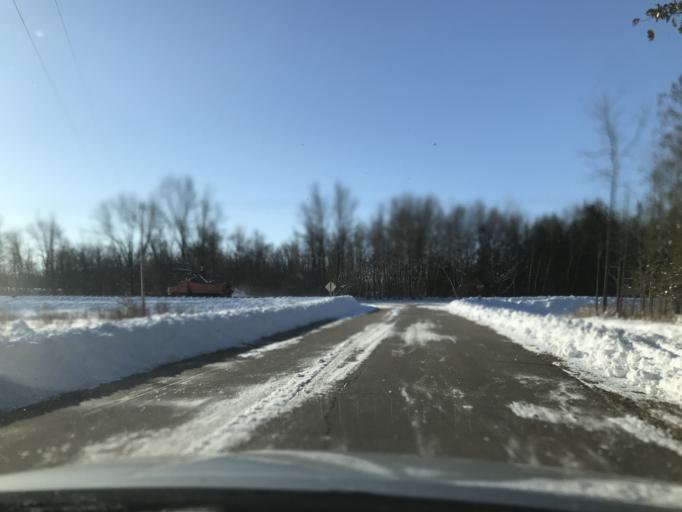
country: US
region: Wisconsin
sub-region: Oconto County
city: Oconto
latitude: 44.9509
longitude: -87.9771
